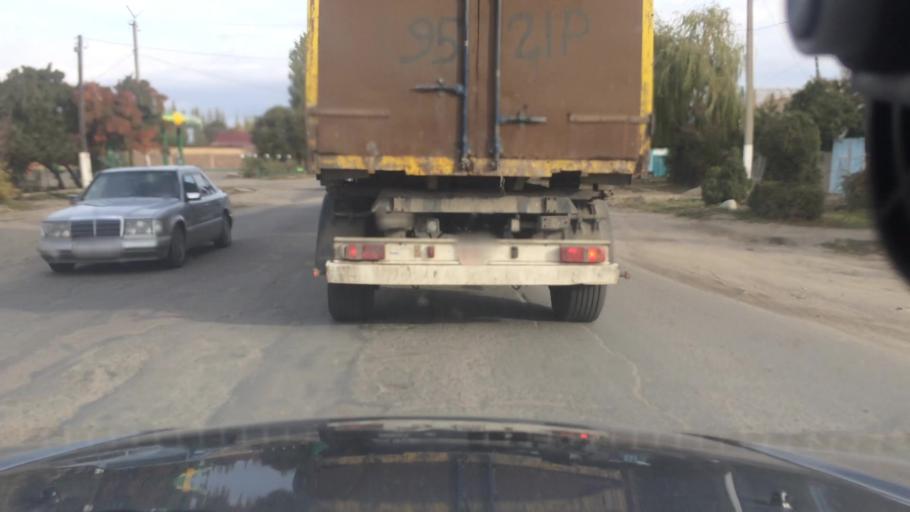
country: KG
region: Ysyk-Koel
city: Karakol
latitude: 42.5173
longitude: 78.3858
